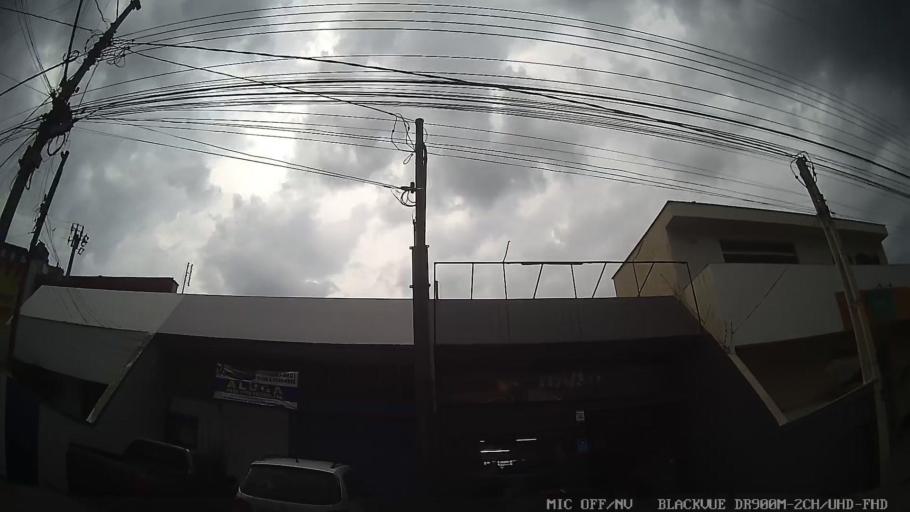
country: BR
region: Sao Paulo
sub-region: Amparo
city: Amparo
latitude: -22.6977
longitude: -46.7622
